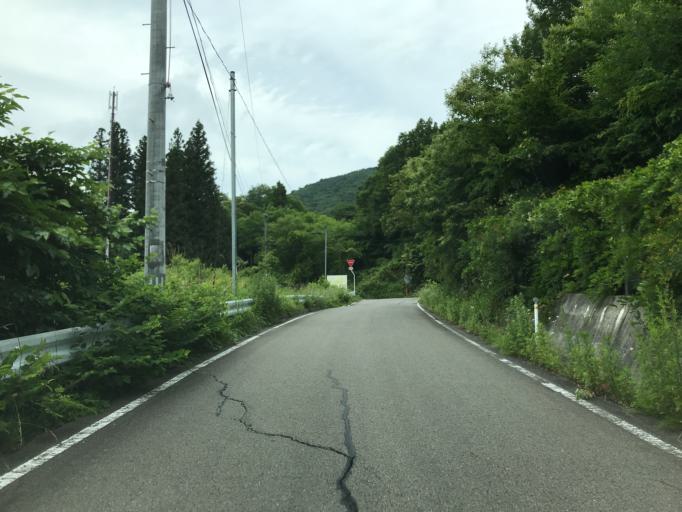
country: JP
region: Fukushima
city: Funehikimachi-funehiki
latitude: 37.4269
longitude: 140.7357
